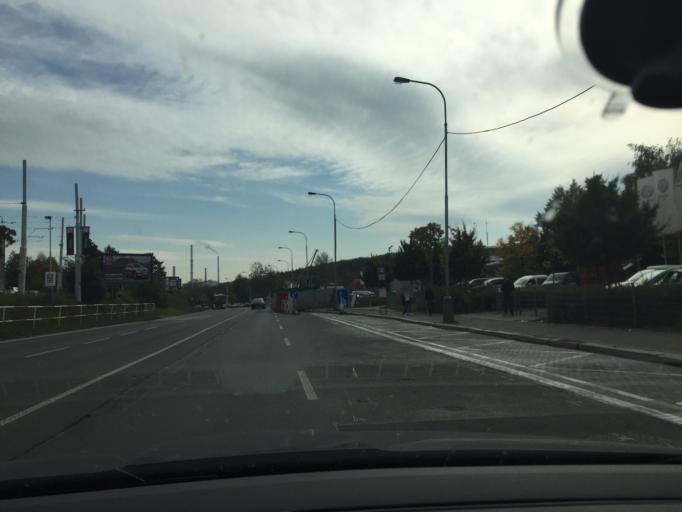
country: CZ
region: Praha
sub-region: Praha 9
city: Prosek
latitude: 50.0916
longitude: 14.4988
